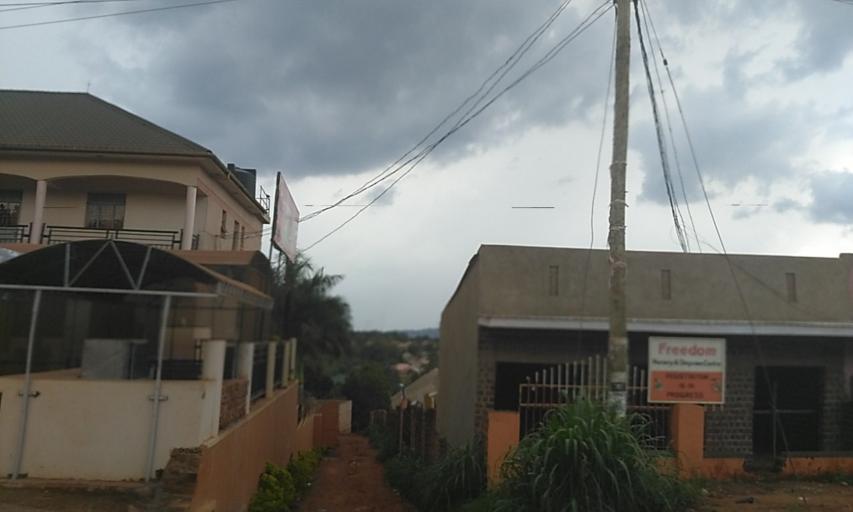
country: UG
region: Central Region
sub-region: Wakiso District
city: Wakiso
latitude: 0.3321
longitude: 32.4943
